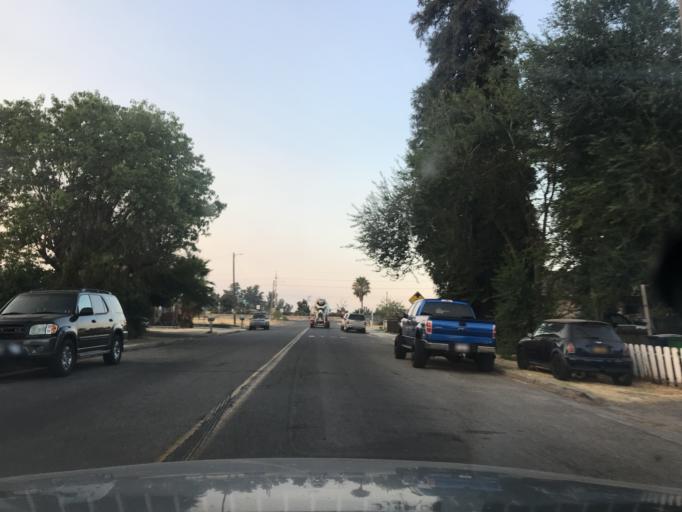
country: US
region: California
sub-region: Merced County
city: Merced
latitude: 37.3185
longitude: -120.5282
